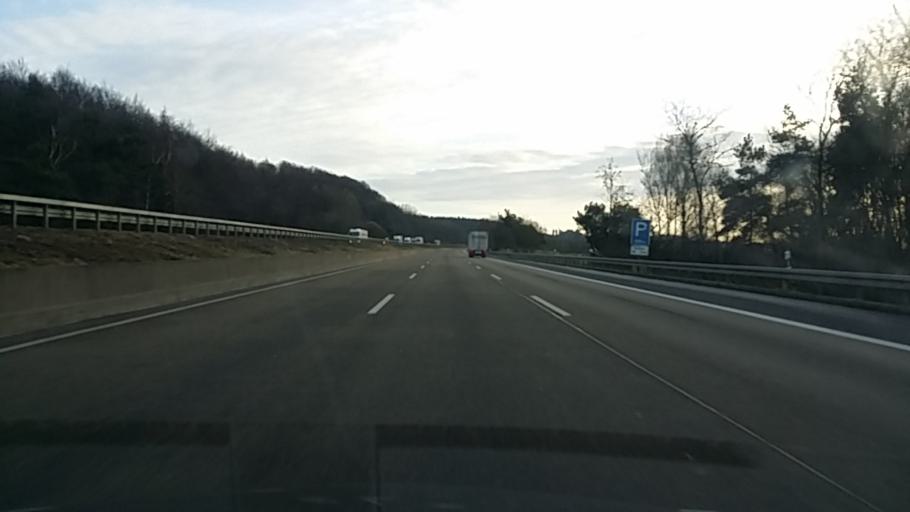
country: DE
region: Bavaria
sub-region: Regierungsbezirk Unterfranken
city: Motten
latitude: 50.3913
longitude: 9.7327
